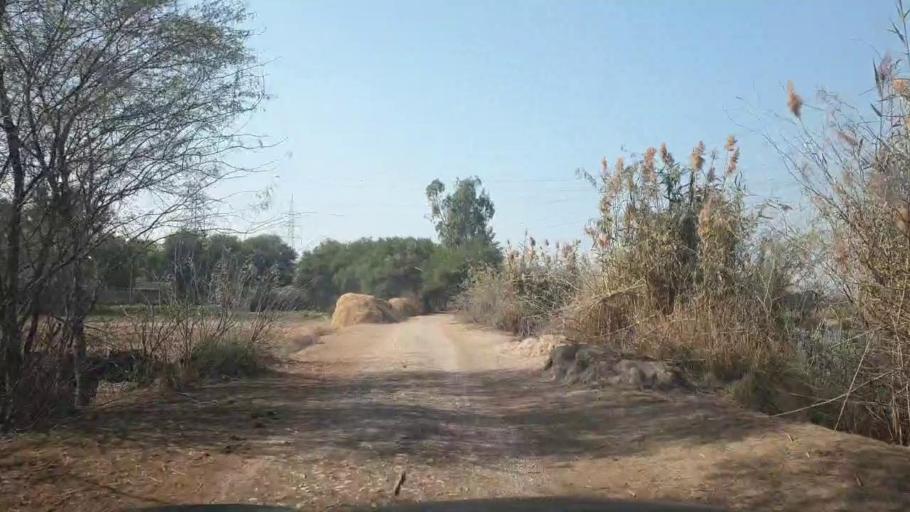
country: PK
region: Sindh
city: Mirpur Mathelo
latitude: 27.9874
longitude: 69.4725
